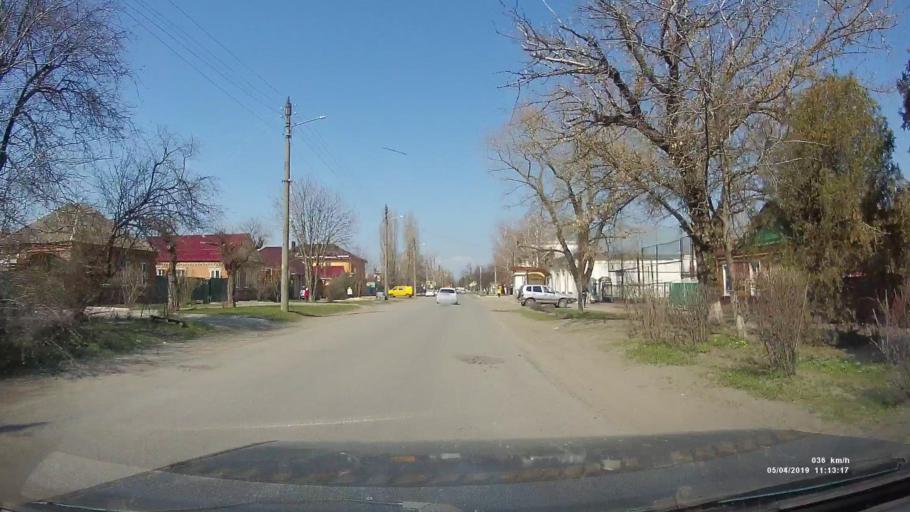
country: RU
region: Rostov
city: Azov
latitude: 47.1015
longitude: 39.4323
